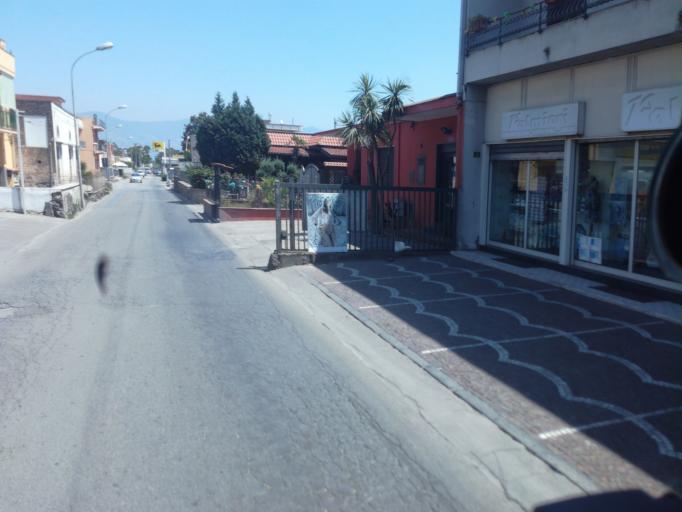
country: IT
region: Campania
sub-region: Provincia di Napoli
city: Boscoreale
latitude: 40.7859
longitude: 14.5135
